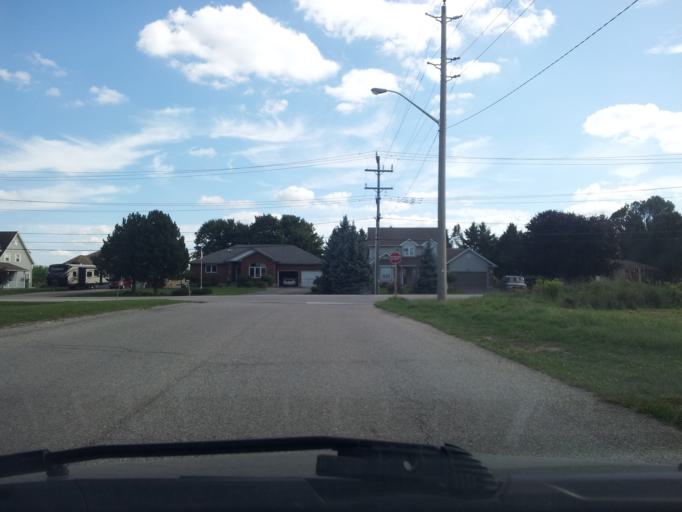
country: CA
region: Ontario
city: Kitchener
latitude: 43.3764
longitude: -80.6915
